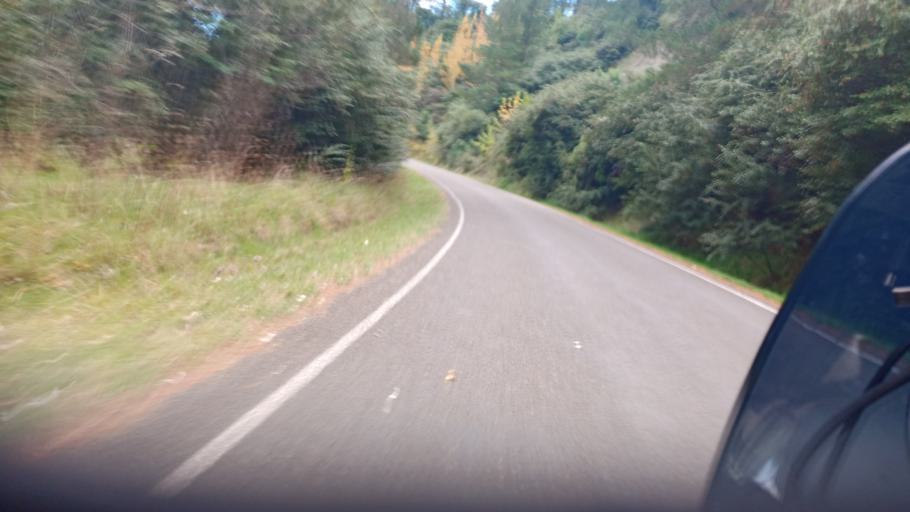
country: NZ
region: Gisborne
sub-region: Gisborne District
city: Gisborne
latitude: -38.4262
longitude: 177.7347
